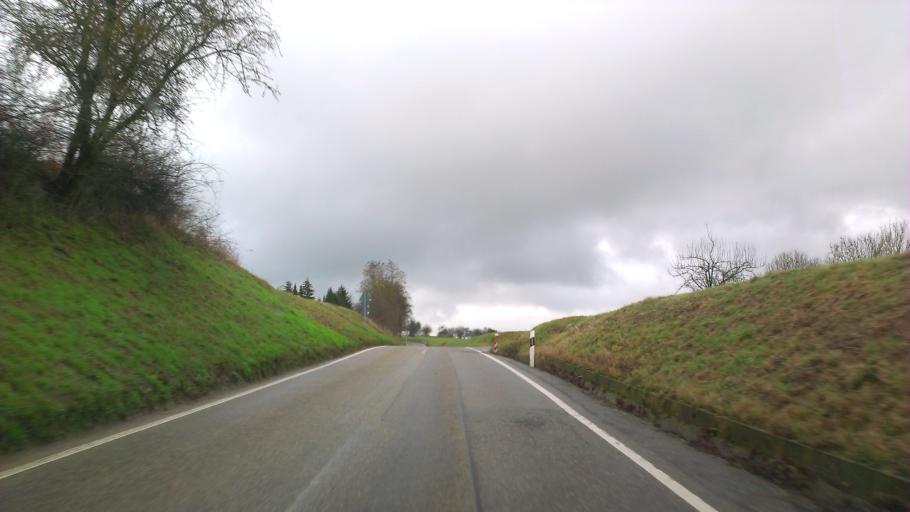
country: DE
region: Baden-Wuerttemberg
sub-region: Karlsruhe Region
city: Zaisenhausen
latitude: 49.1046
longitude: 8.7615
